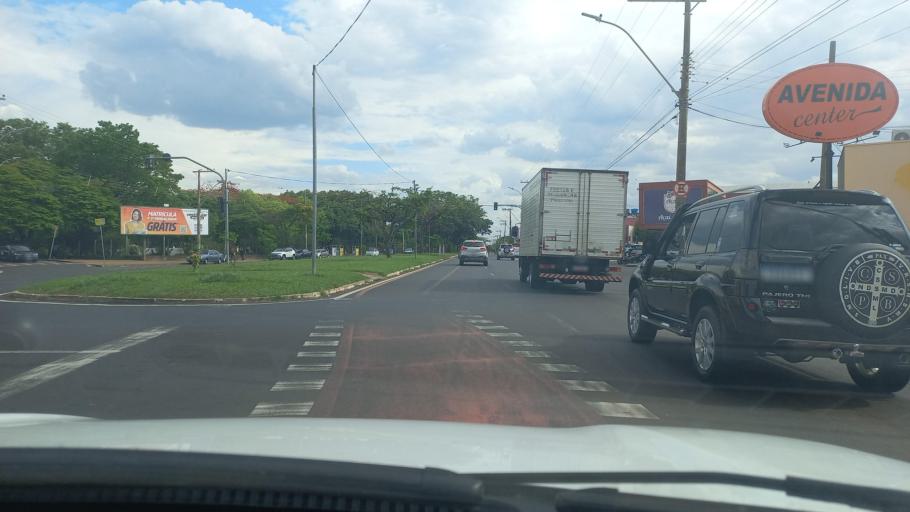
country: BR
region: Minas Gerais
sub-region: Uberaba
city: Uberaba
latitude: -19.7540
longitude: -47.9646
